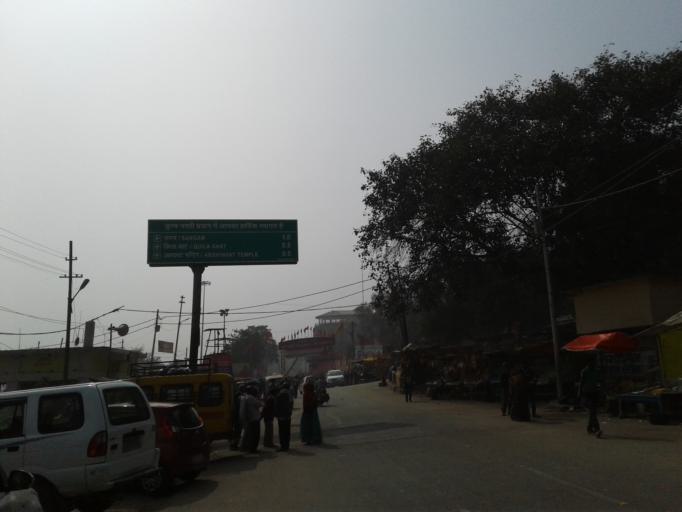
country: IN
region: Uttar Pradesh
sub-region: Allahabad
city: Jhusi
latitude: 25.4345
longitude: 81.8796
